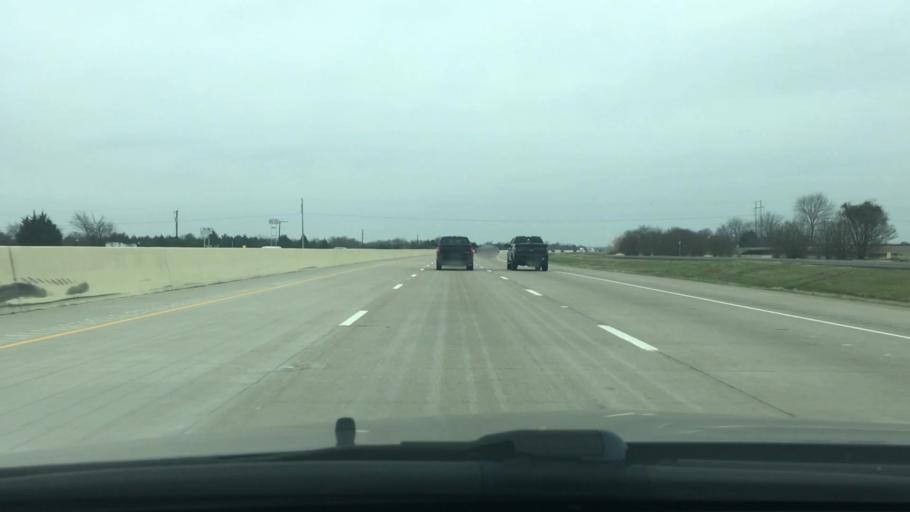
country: US
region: Texas
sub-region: Navarro County
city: Corsicana
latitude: 31.9876
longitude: -96.4252
